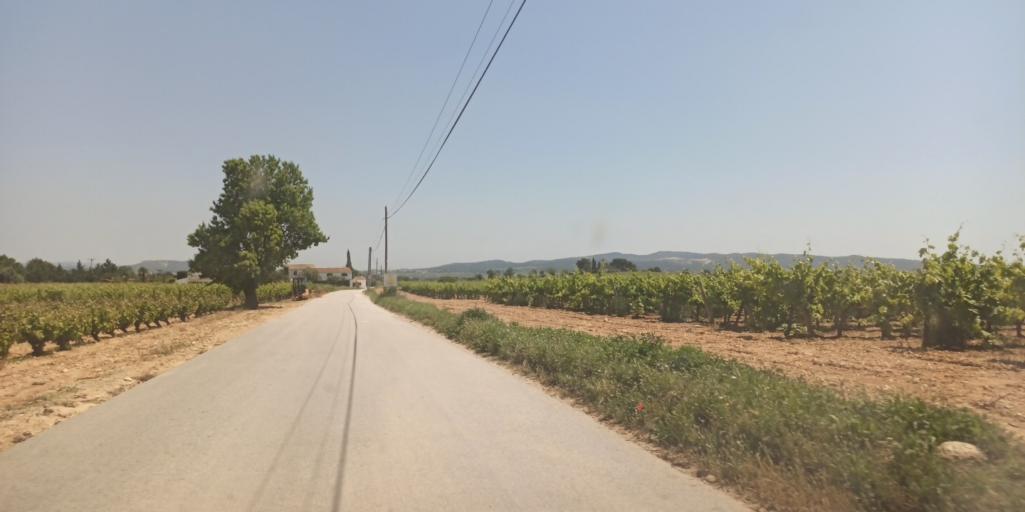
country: ES
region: Catalonia
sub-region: Provincia de Barcelona
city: Vilobi del Penedes
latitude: 41.3566
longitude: 1.6390
